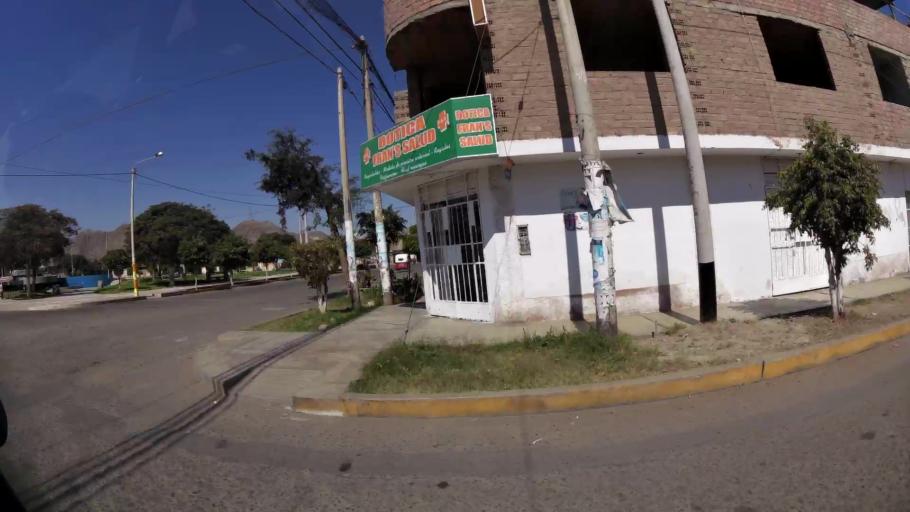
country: PE
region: Ica
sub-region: Provincia de Ica
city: La Tinguina
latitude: -14.0468
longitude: -75.6993
